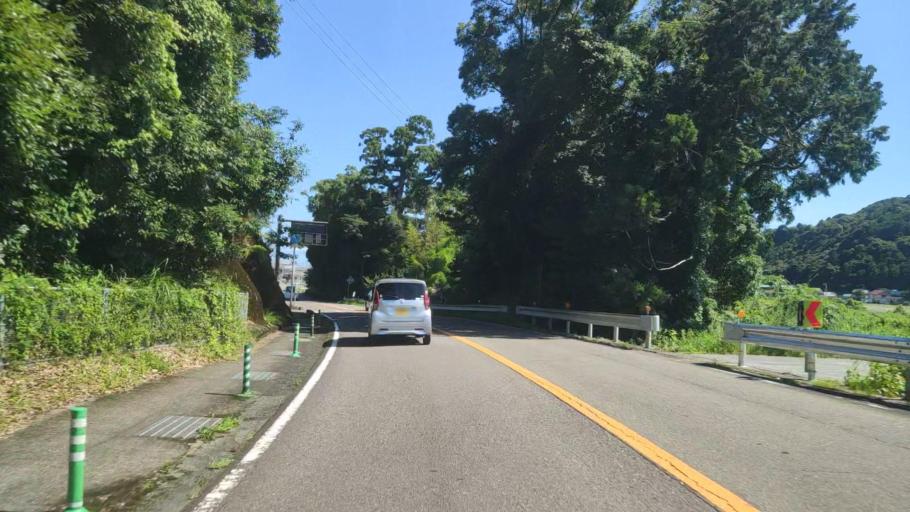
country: JP
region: Wakayama
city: Shingu
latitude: 33.5855
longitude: 135.9184
